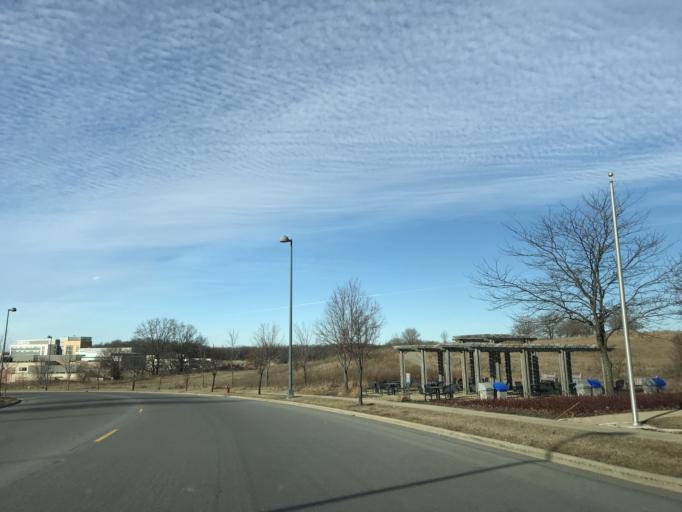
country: US
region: Wisconsin
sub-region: Dane County
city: Windsor
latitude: 43.1515
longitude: -89.2939
